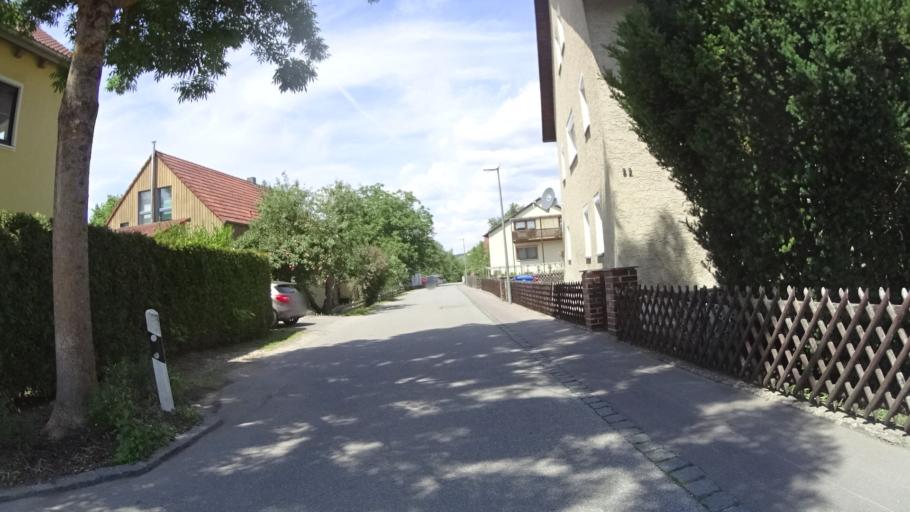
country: DE
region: Bavaria
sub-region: Lower Bavaria
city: Bad Abbach
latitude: 48.9457
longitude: 12.0229
